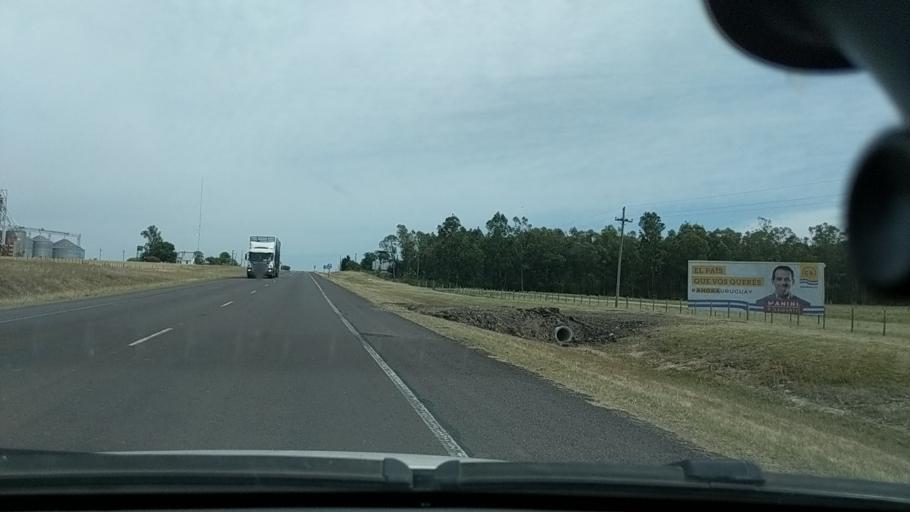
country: UY
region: Durazno
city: Durazno
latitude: -33.4513
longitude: -56.4722
